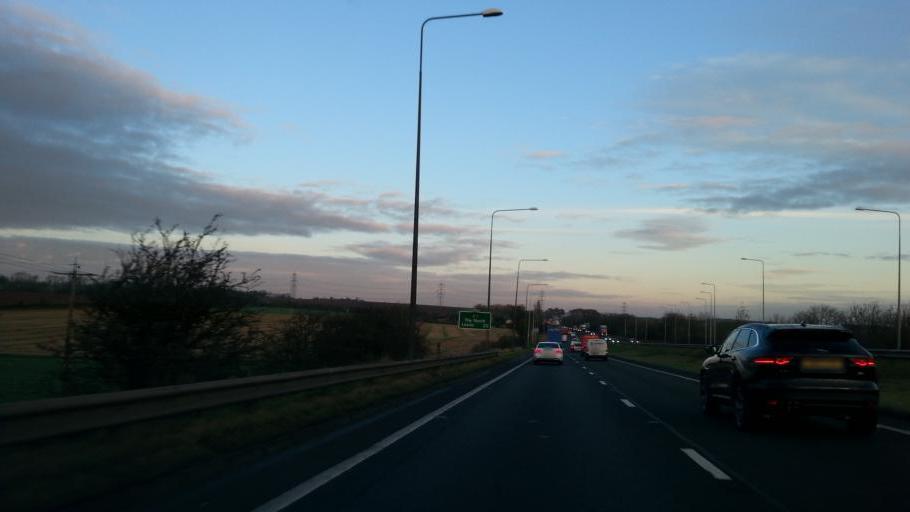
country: GB
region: England
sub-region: Doncaster
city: Norton
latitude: 53.6194
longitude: -1.2322
